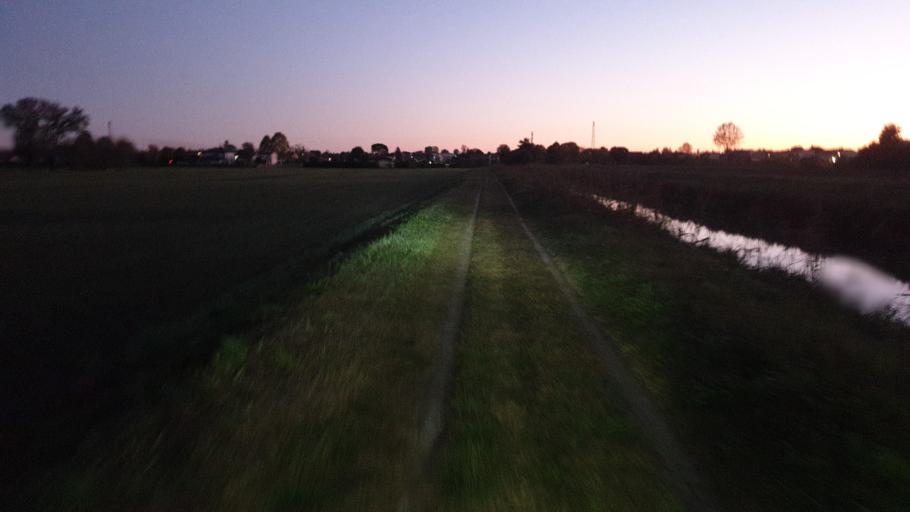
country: IT
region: Veneto
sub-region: Provincia di Venezia
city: Stra
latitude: 45.4243
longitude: 12.0100
